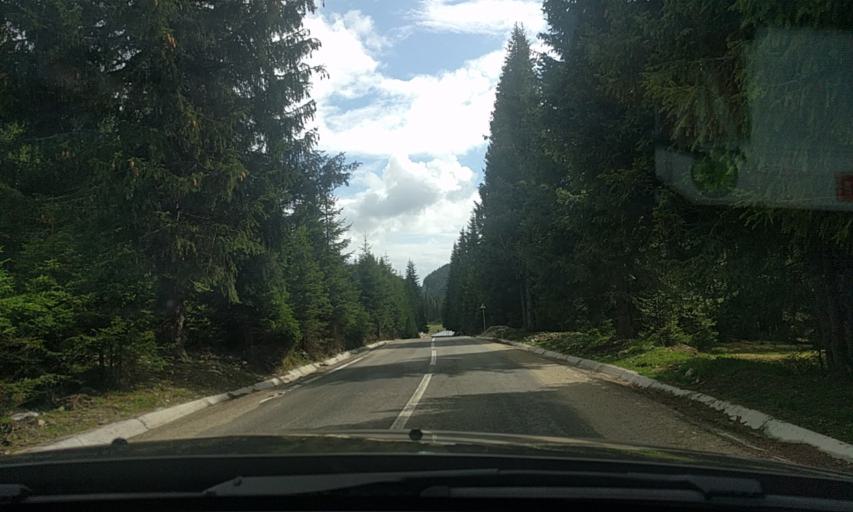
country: RO
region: Prahova
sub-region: Oras Busteni
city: Busteni
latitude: 45.3809
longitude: 25.4385
